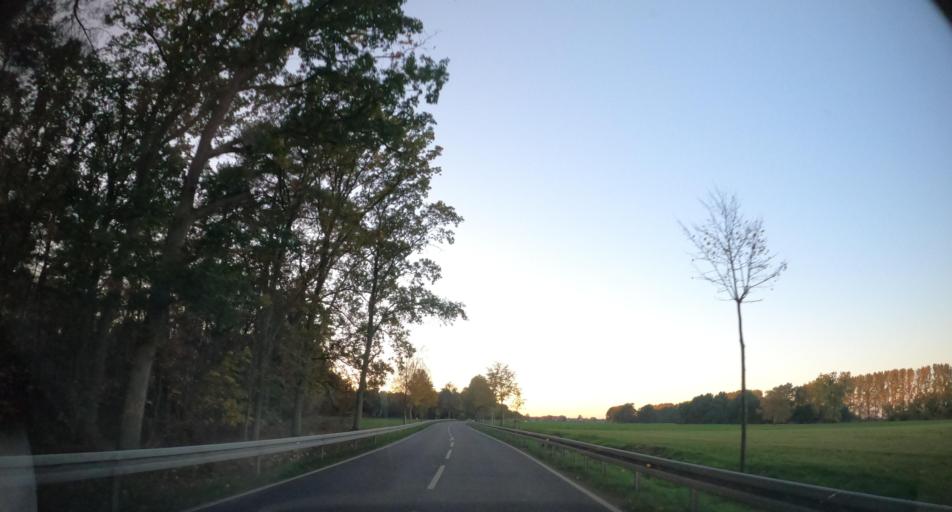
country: DE
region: Mecklenburg-Vorpommern
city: Ueckermunde
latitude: 53.7642
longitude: 13.9916
